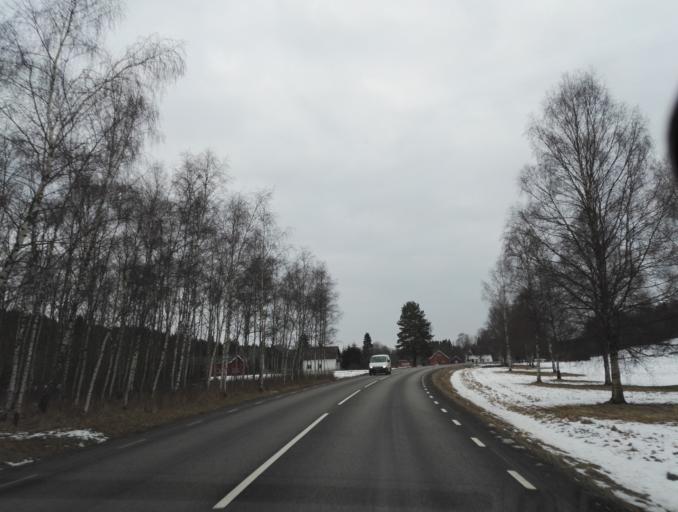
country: SE
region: Vaestra Goetaland
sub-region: Bollebygds Kommun
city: Bollebygd
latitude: 57.6964
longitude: 12.5708
